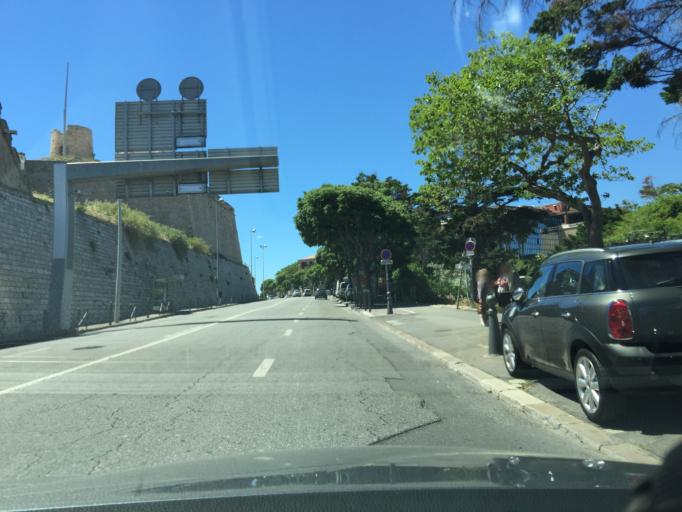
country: FR
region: Provence-Alpes-Cote d'Azur
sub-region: Departement des Bouches-du-Rhone
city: Marseille 02
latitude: 43.2922
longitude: 5.3624
